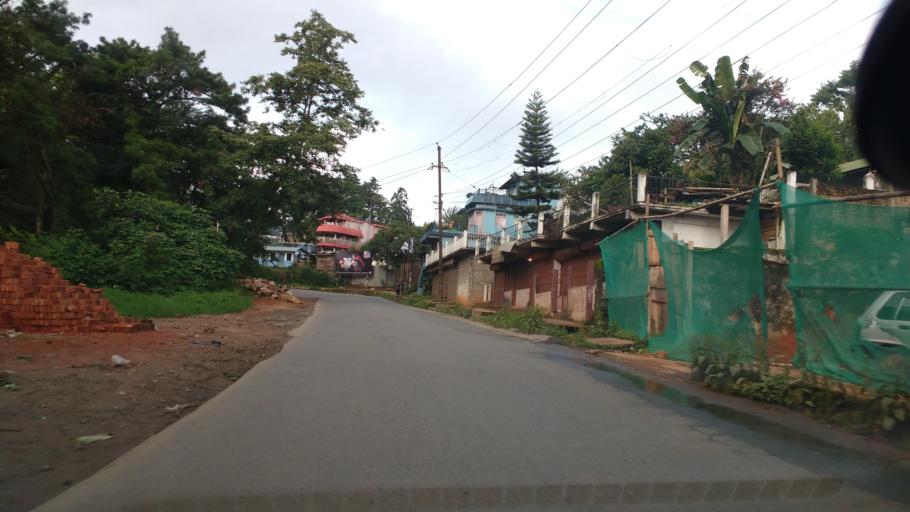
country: IN
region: Meghalaya
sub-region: East Khasi Hills
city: Shillong
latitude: 25.5643
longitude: 91.8546
